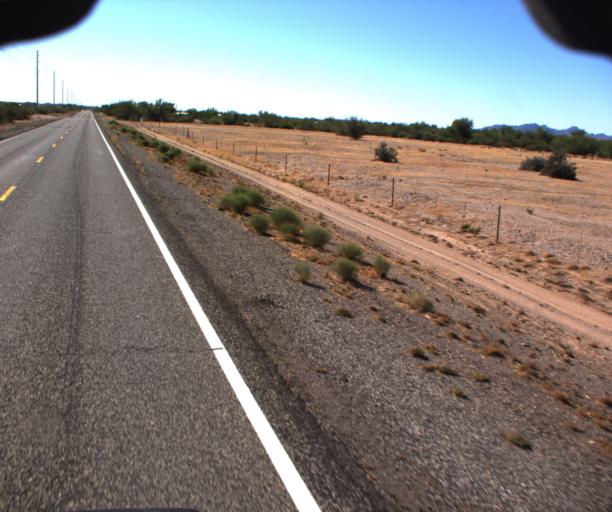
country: US
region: Arizona
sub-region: La Paz County
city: Cienega Springs
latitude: 33.9551
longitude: -114.0259
